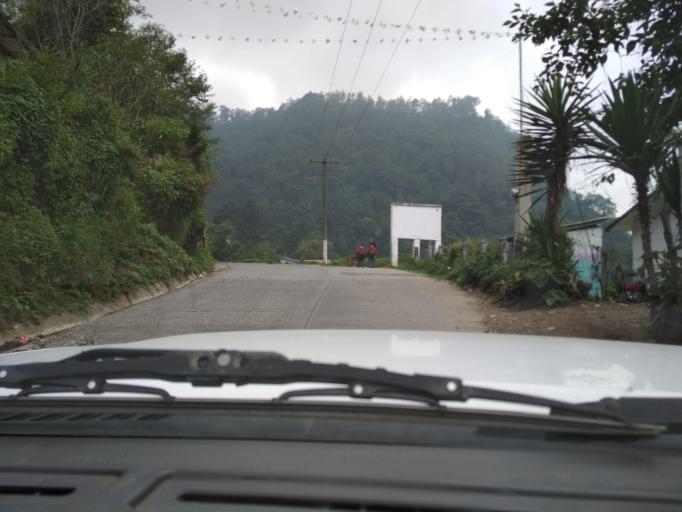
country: MX
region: Veracruz
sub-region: La Perla
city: Metlac Hernandez (Metlac Primero)
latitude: 18.9765
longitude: -97.1437
